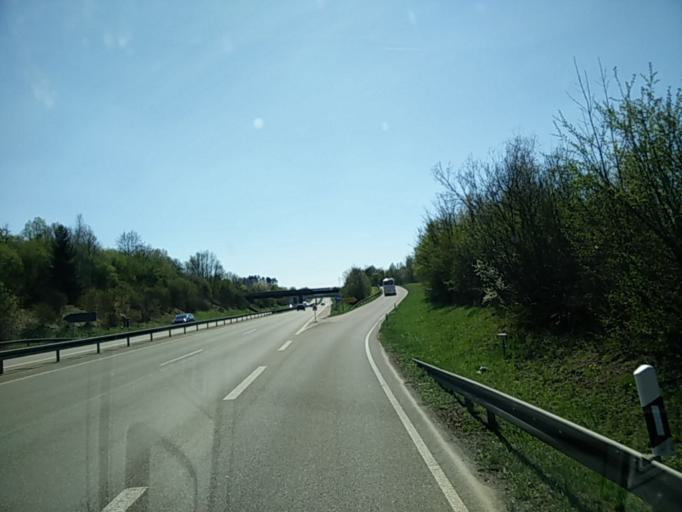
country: DE
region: Baden-Wuerttemberg
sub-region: Tuebingen Region
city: Bodelshausen
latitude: 48.3876
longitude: 8.9962
